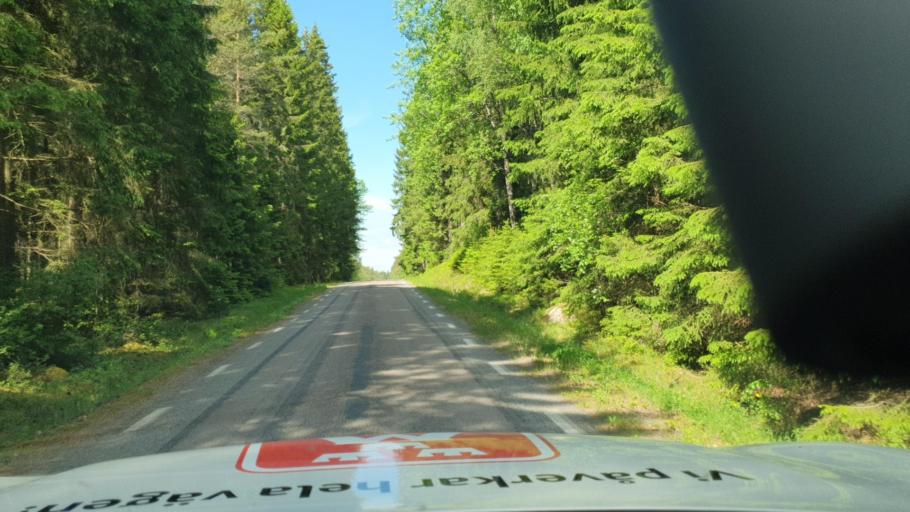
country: SE
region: Vaestra Goetaland
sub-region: Herrljunga Kommun
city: Herrljunga
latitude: 58.1233
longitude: 13.0956
